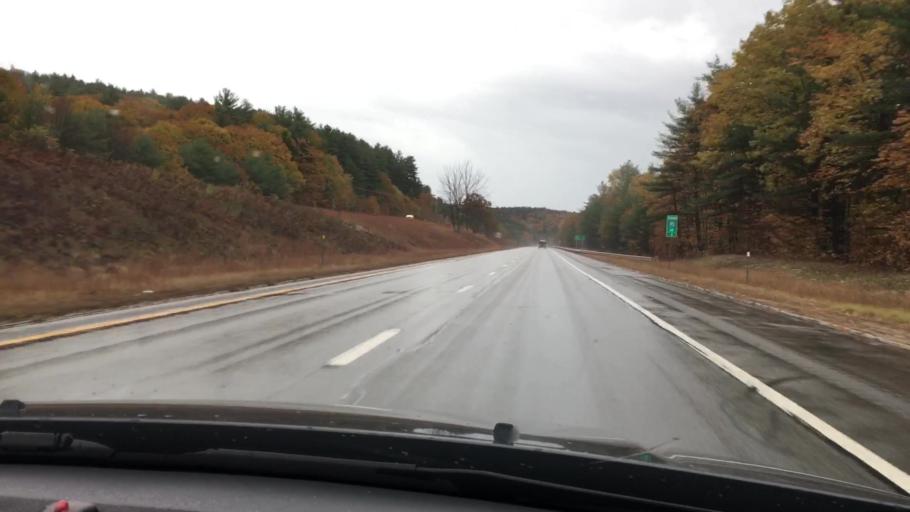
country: US
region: New Hampshire
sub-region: Grafton County
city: Ashland
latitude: 43.6058
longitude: -71.6373
